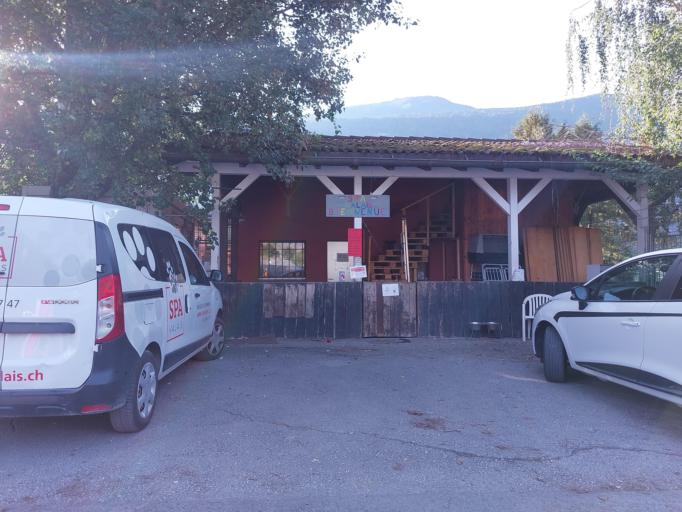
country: CH
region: Valais
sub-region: Conthey District
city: Ardon
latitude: 46.2026
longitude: 7.2644
